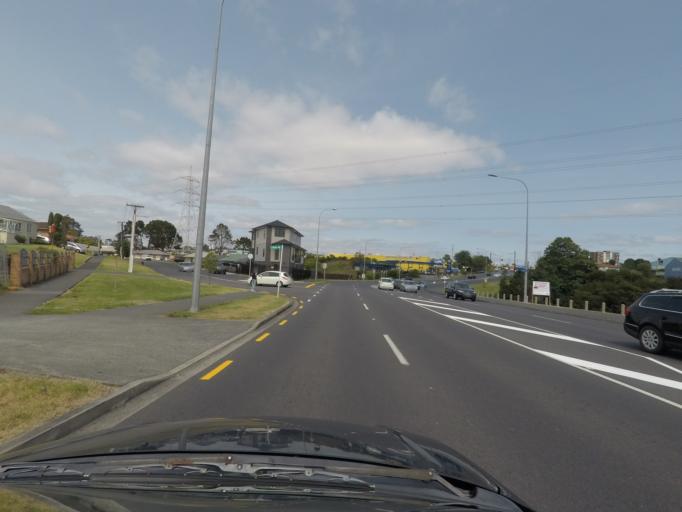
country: NZ
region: Auckland
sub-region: Auckland
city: Waitakere
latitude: -36.9104
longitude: 174.6925
